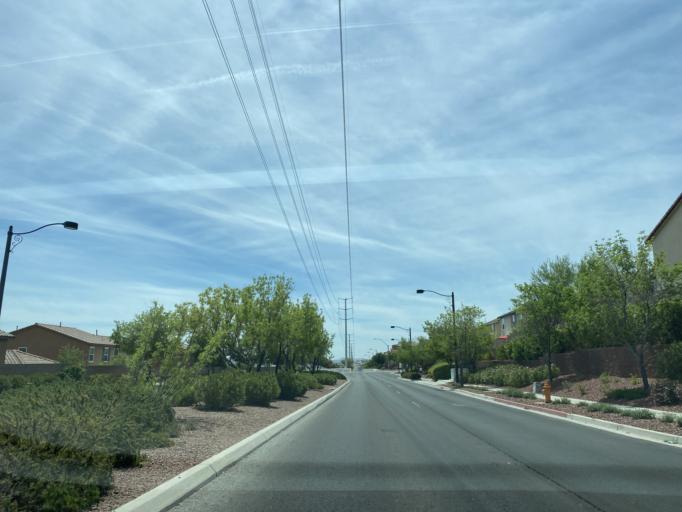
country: US
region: Nevada
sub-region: Clark County
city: Summerlin South
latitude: 36.2930
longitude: -115.3220
